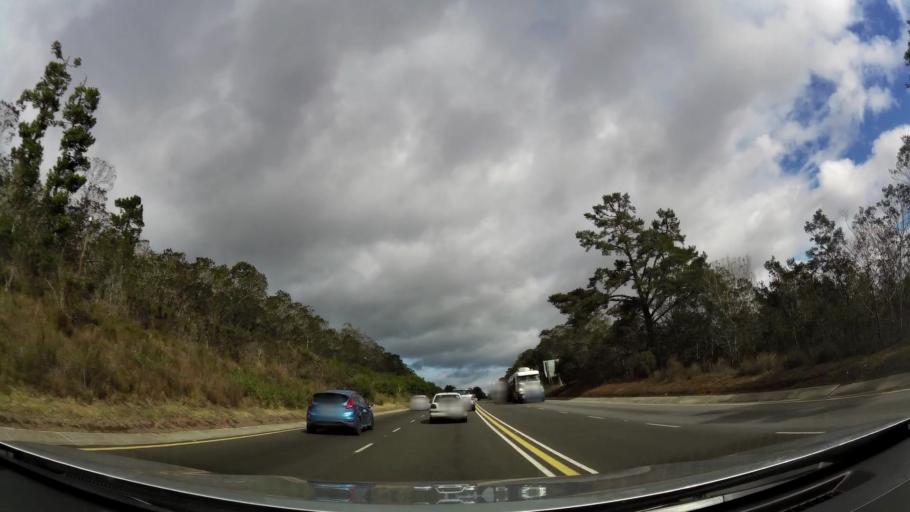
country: ZA
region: Western Cape
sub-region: Eden District Municipality
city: George
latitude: -33.9903
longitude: 22.5381
